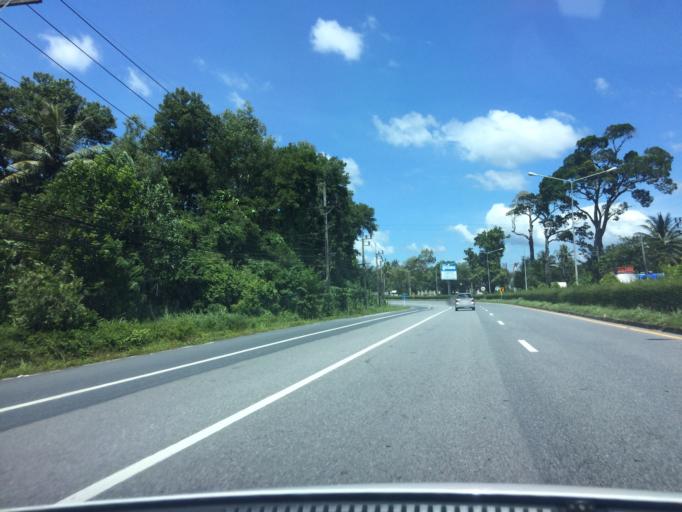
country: TH
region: Phangnga
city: Thai Mueang
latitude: 8.2262
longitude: 98.2997
